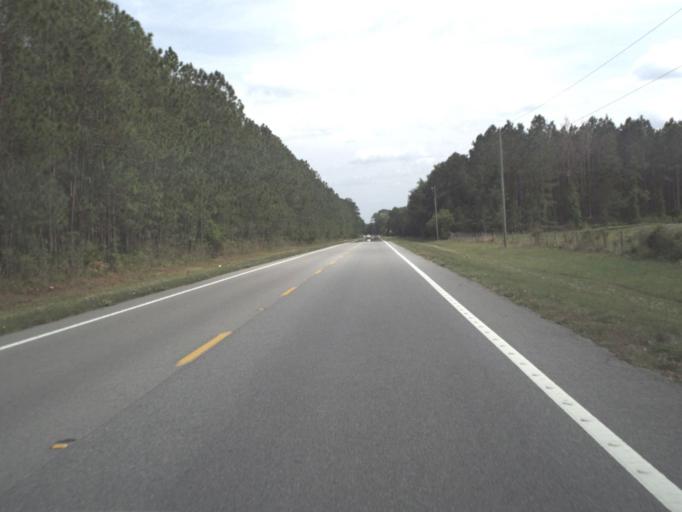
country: US
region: Florida
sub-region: Putnam County
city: Crescent City
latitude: 29.5198
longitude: -81.5055
